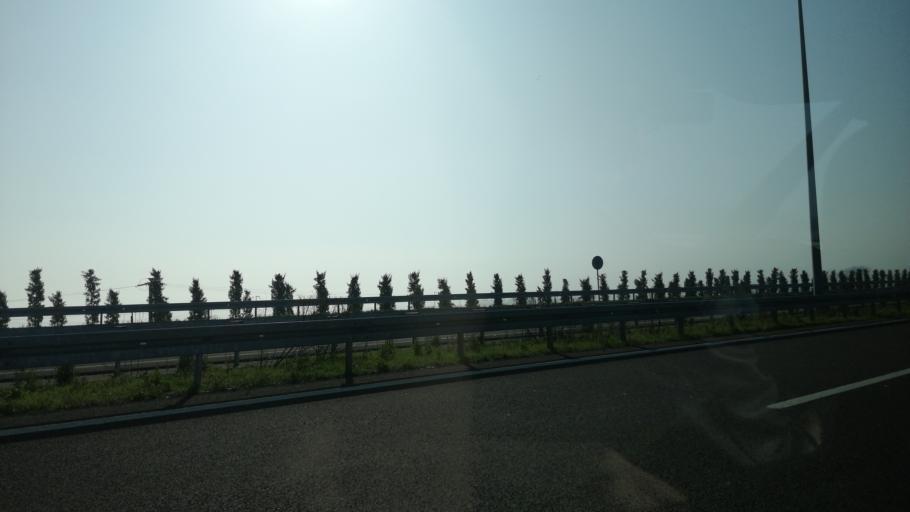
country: TR
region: Yalova
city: Altinova
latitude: 40.7195
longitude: 29.5021
